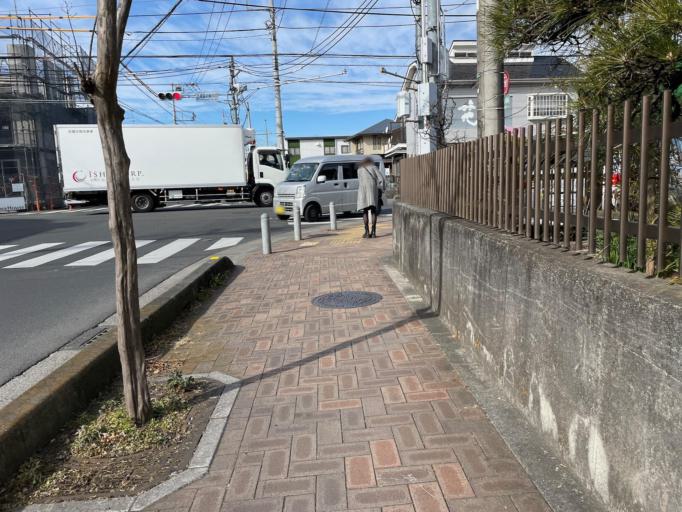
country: JP
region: Saitama
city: Sayama
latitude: 35.8228
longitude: 139.4079
